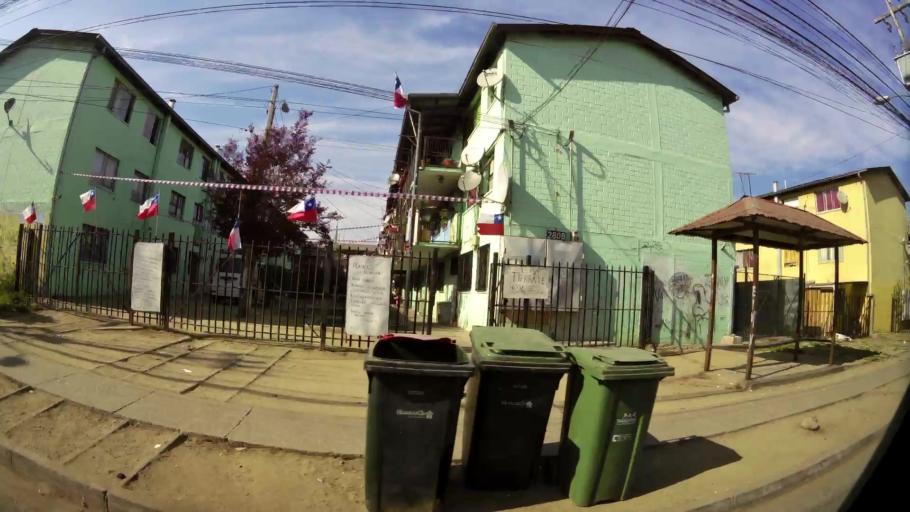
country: CL
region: Santiago Metropolitan
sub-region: Provincia de Talagante
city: Talagante
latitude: -33.6786
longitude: -70.9453
